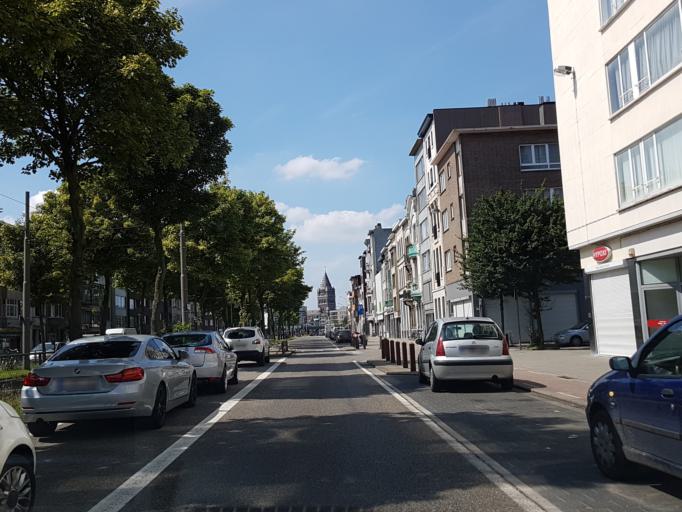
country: BE
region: Flanders
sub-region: Provincie Antwerpen
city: Borsbeek
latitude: 51.2114
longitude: 4.4510
